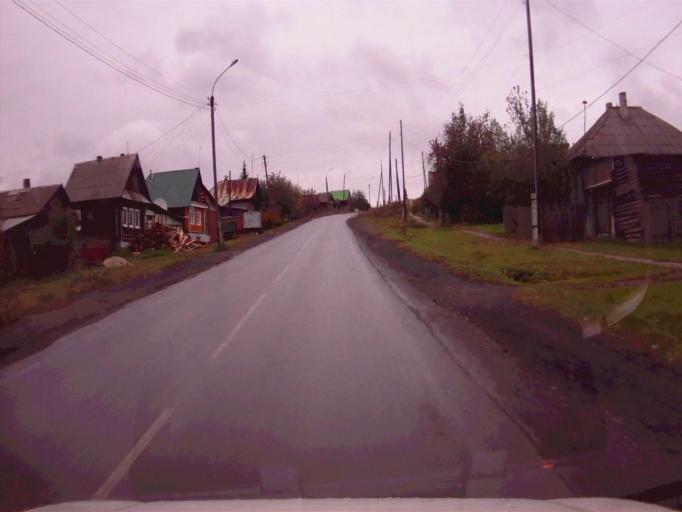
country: RU
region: Chelyabinsk
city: Verkhniy Ufaley
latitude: 56.0514
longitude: 60.2052
